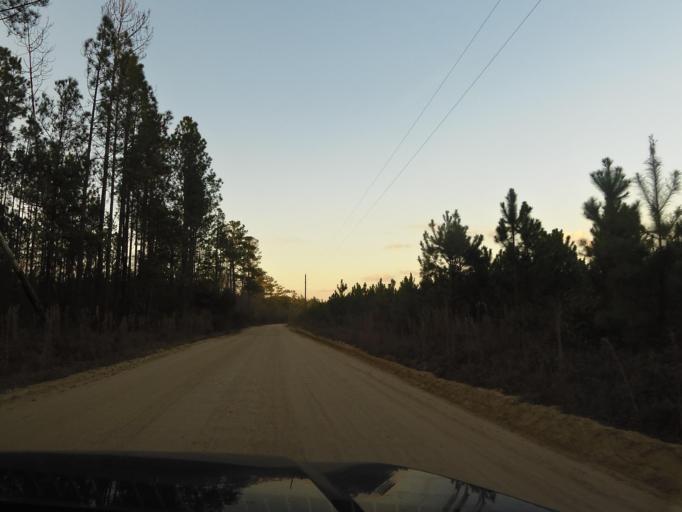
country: US
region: Florida
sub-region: Clay County
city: Green Cove Springs
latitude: 29.8787
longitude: -81.7928
